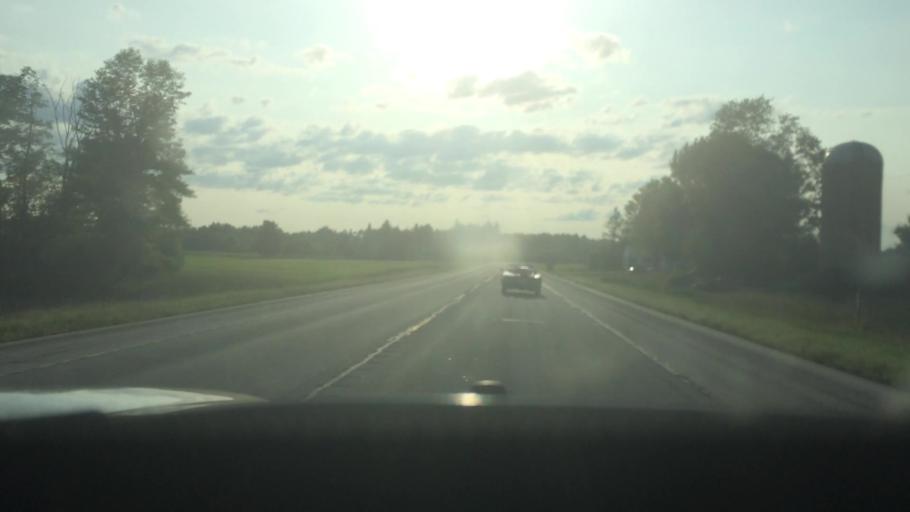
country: US
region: New York
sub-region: St. Lawrence County
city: Canton
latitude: 44.6359
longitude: -75.2663
